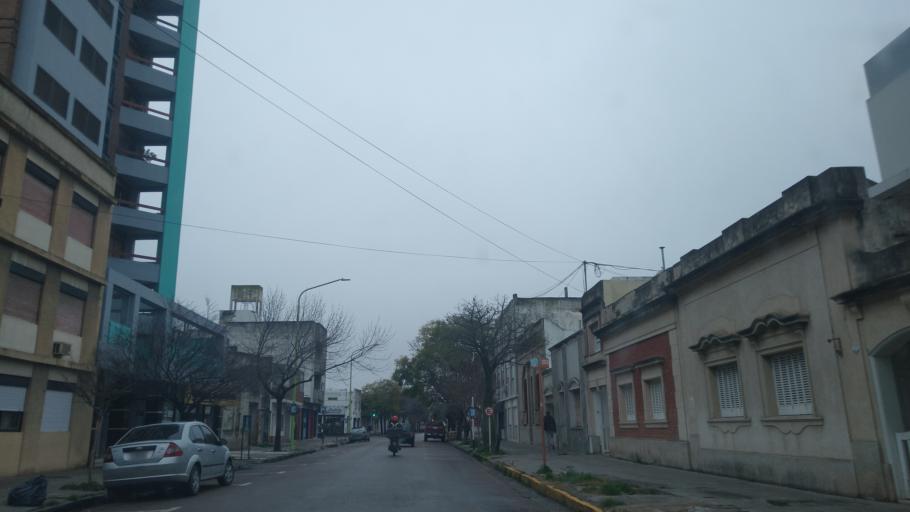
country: AR
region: Buenos Aires
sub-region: Partido de Bahia Blanca
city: Bahia Blanca
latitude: -38.7124
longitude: -62.2675
